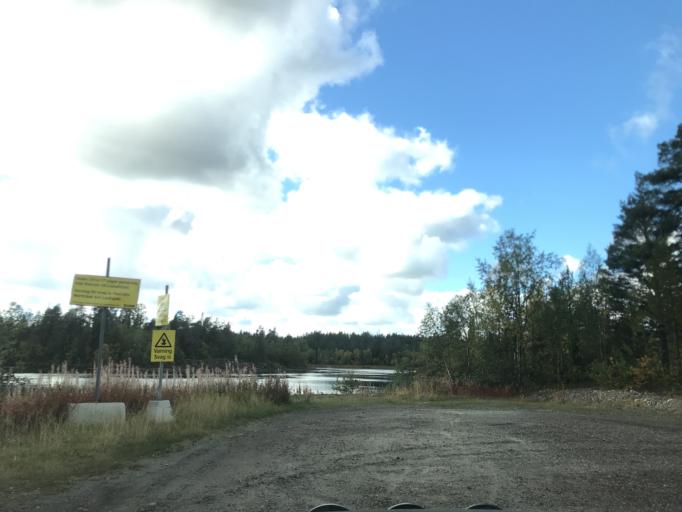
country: SE
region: Norrbotten
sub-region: Gallivare Kommun
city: Malmberget
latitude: 67.5837
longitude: 20.8539
